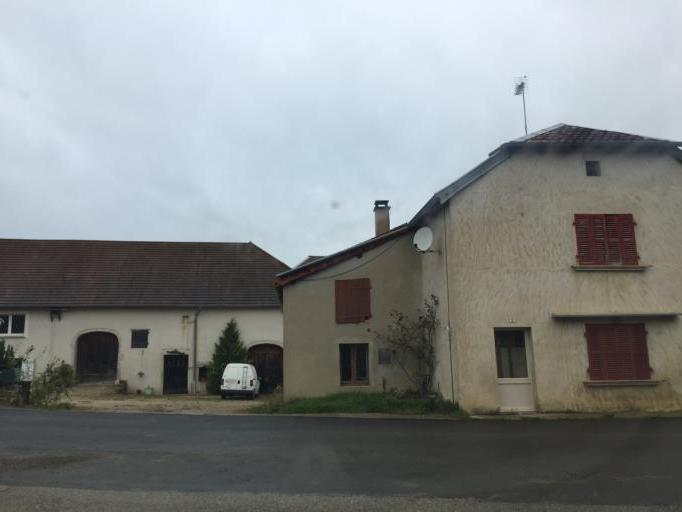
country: FR
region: Franche-Comte
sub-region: Departement du Jura
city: Orgelet
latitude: 46.5077
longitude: 5.5668
